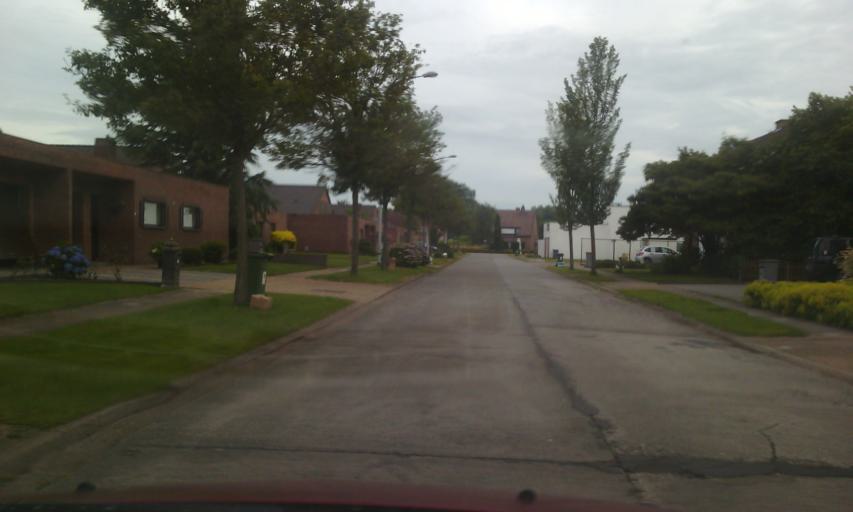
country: BE
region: Flanders
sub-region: Provincie Oost-Vlaanderen
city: Zele
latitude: 51.0714
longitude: 4.0300
